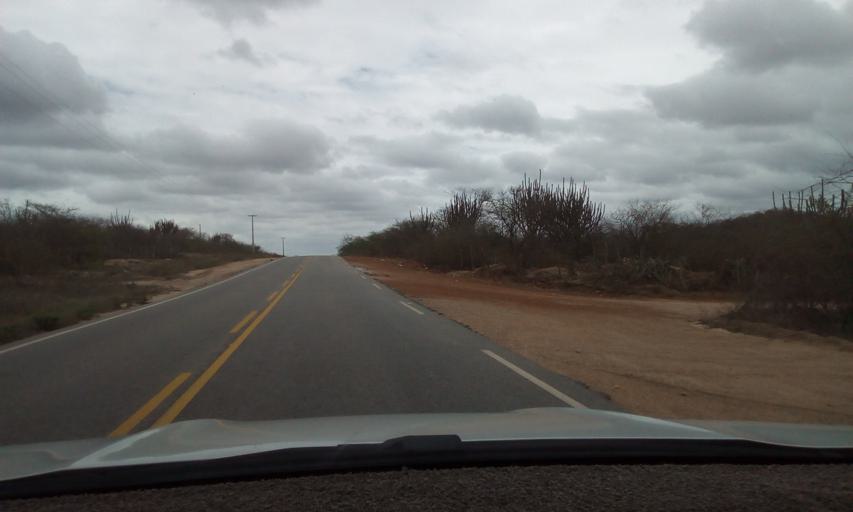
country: BR
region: Paraiba
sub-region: Picui
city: Picui
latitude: -6.5630
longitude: -36.2815
